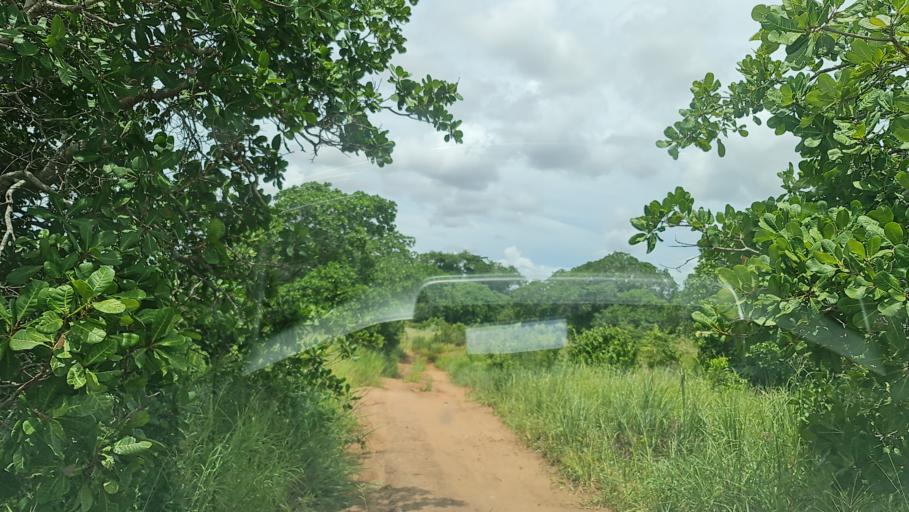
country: MZ
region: Nampula
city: Nacala
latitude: -14.7873
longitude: 39.9743
